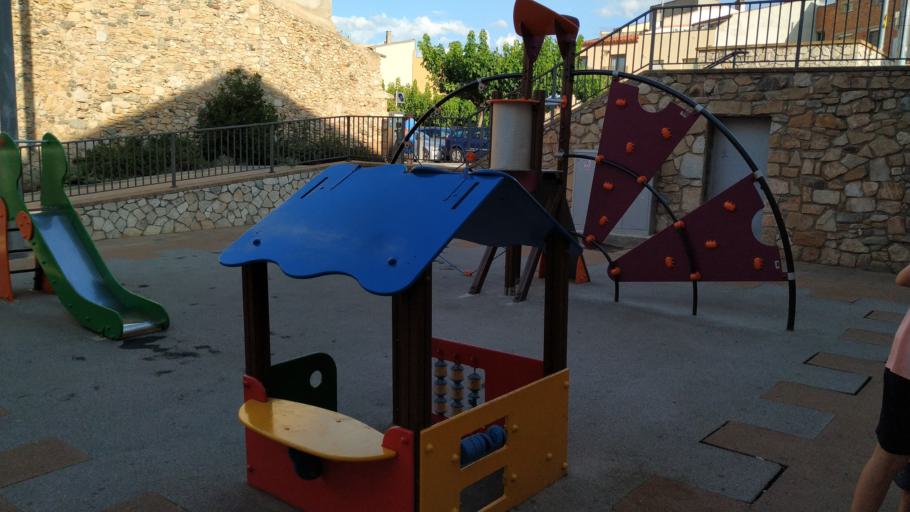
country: ES
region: Catalonia
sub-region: Provincia de Tarragona
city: Montblanc
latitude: 41.3761
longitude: 1.1629
